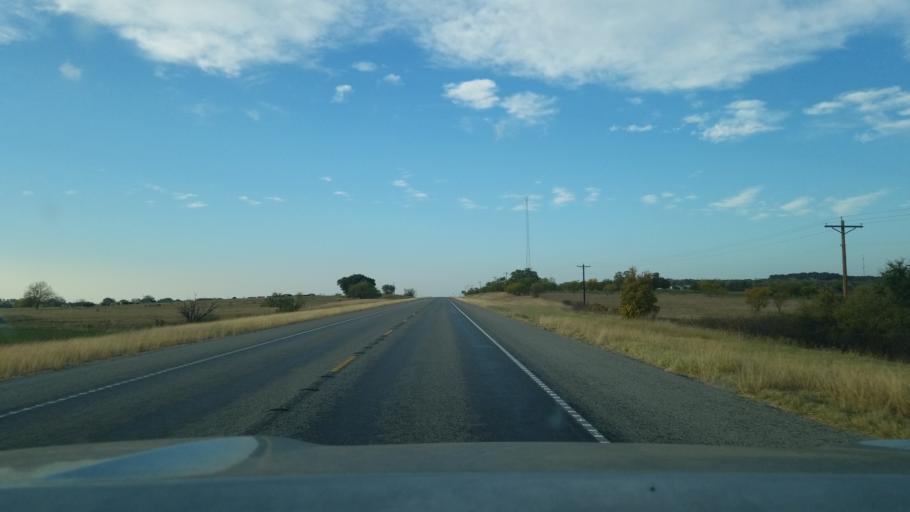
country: US
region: Texas
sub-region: Brown County
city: Lake Brownwood
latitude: 32.0268
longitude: -98.9304
